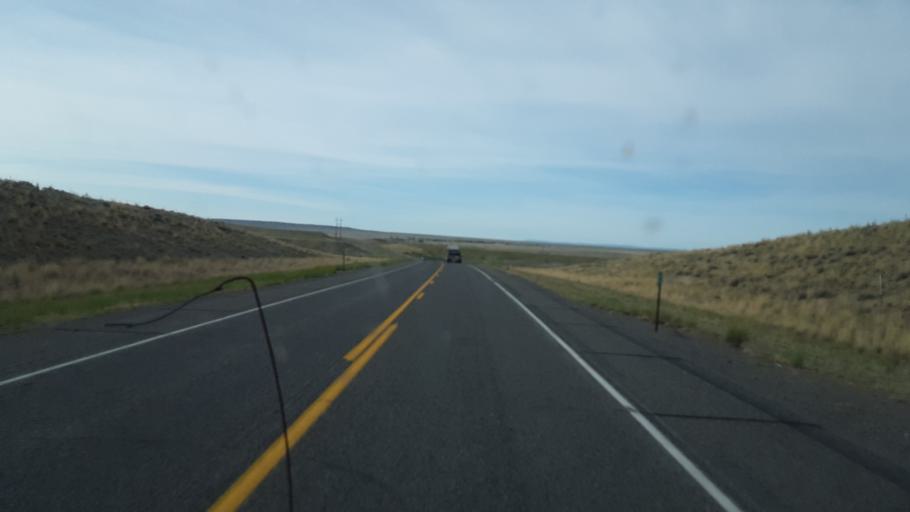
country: US
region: Wyoming
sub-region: Fremont County
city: Riverton
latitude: 43.2896
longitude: -108.1278
